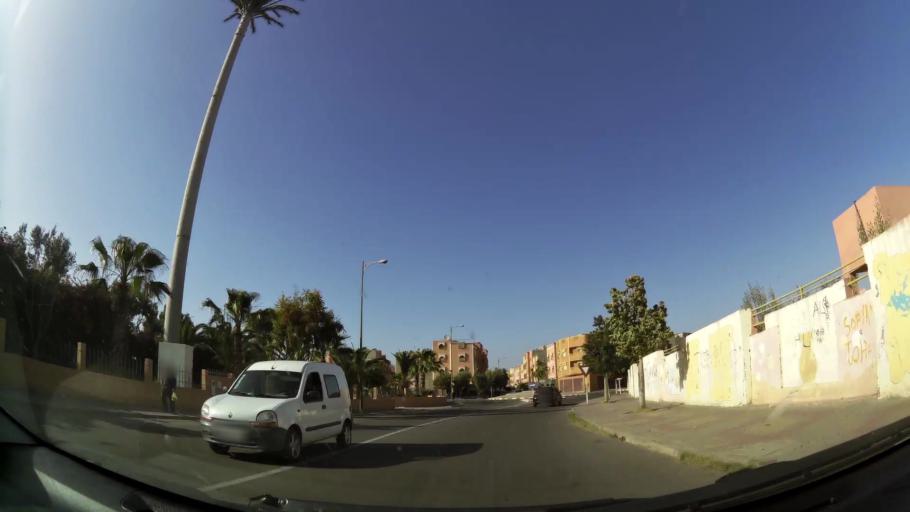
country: MA
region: Souss-Massa-Draa
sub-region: Inezgane-Ait Mellou
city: Inezgane
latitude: 30.3687
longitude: -9.5291
